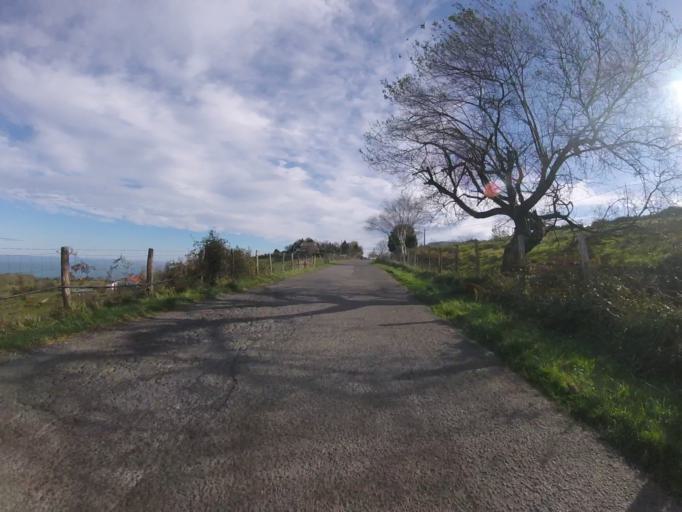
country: ES
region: Basque Country
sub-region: Provincia de Guipuzcoa
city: Orio
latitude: 43.2933
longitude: -2.0953
